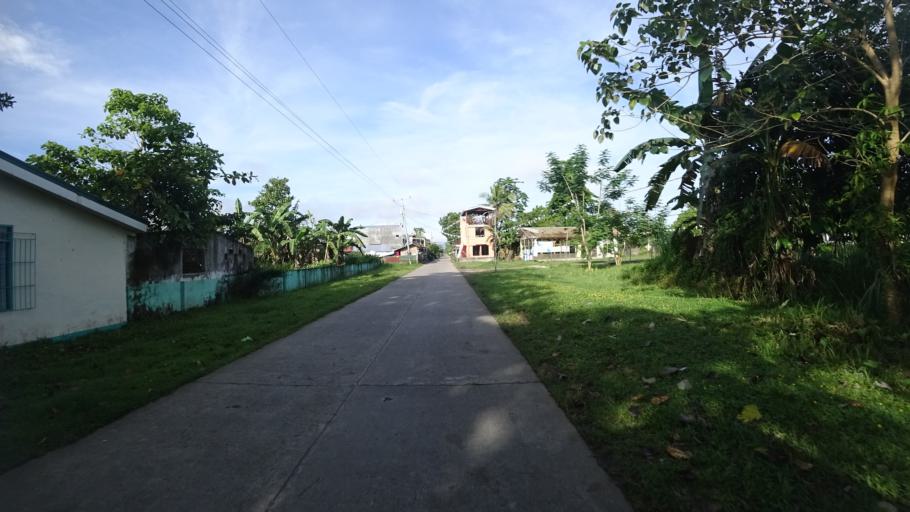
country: PH
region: Eastern Visayas
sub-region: Province of Leyte
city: Santa Fe
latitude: 11.1912
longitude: 124.8805
